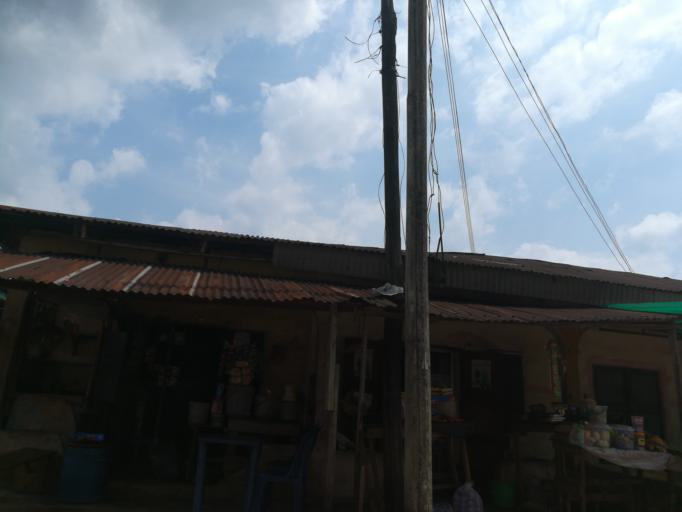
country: NG
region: Rivers
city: Okrika
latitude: 4.7308
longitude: 7.1528
